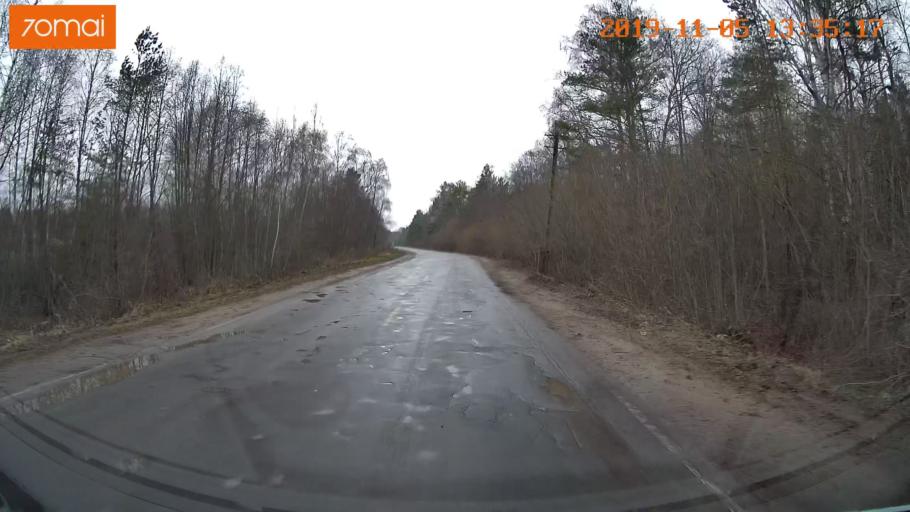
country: RU
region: Ivanovo
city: Shuya
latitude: 56.9068
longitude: 41.3881
